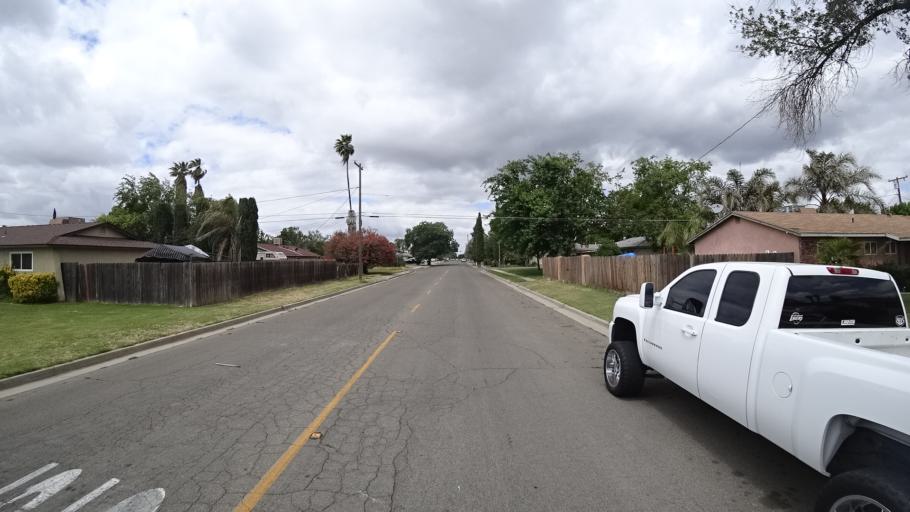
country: US
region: California
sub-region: Kings County
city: Hanford
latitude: 36.3330
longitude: -119.6281
